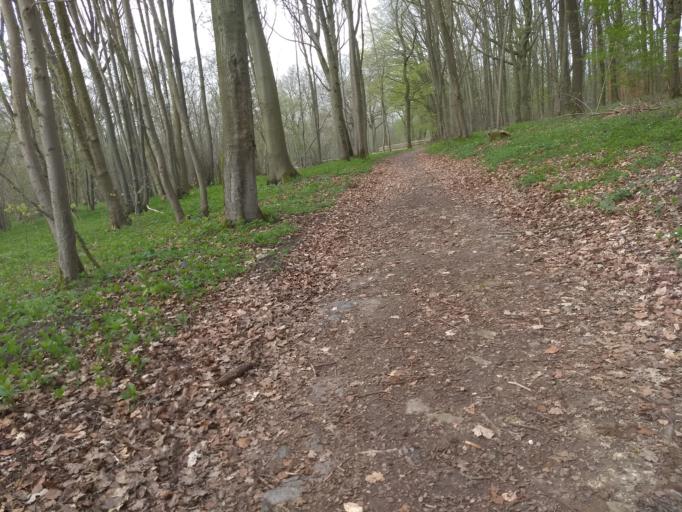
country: FR
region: Nord-Pas-de-Calais
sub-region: Departement du Pas-de-Calais
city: Maroeuil
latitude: 50.3321
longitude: 2.6955
